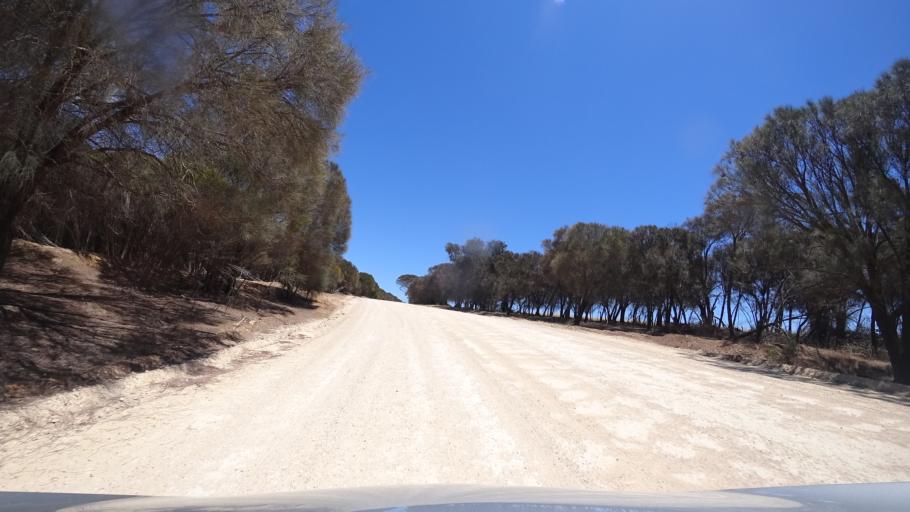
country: AU
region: South Australia
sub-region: Kangaroo Island
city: Kingscote
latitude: -35.6287
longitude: 137.1996
